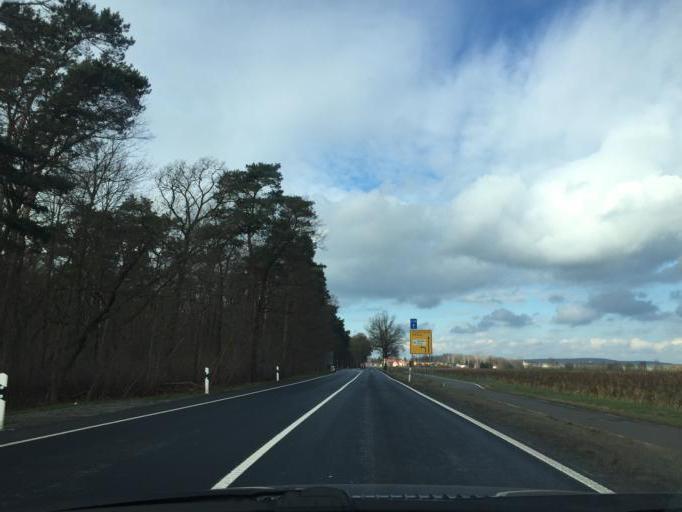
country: DE
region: Saxony
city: Ottendorf-Okrilla
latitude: 51.1741
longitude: 13.8553
